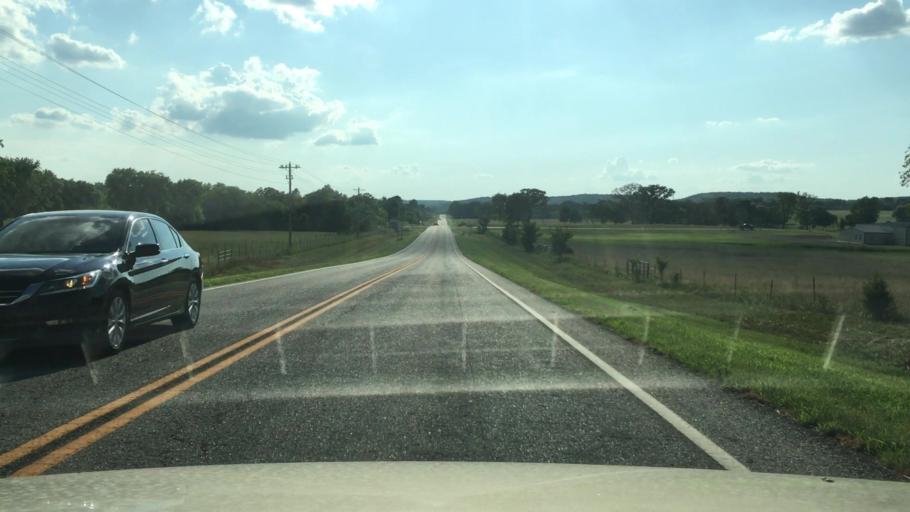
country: US
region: Oklahoma
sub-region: Cherokee County
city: Tahlequah
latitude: 35.9152
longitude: -95.0790
